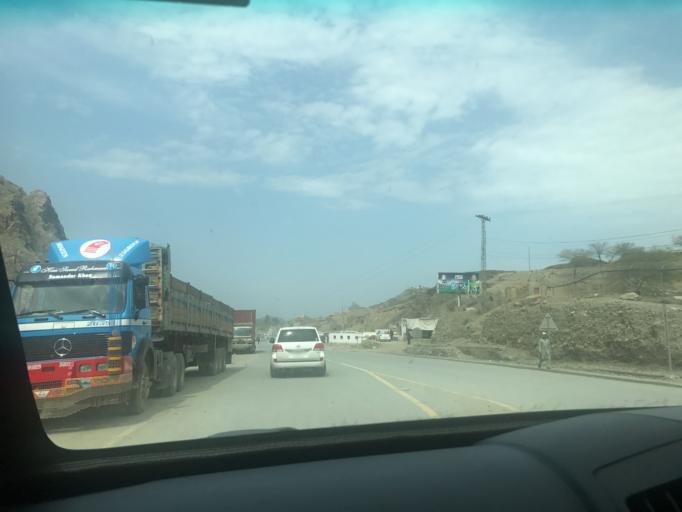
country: PK
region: Federally Administered Tribal Areas
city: Landi Kotal
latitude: 34.1168
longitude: 71.1016
